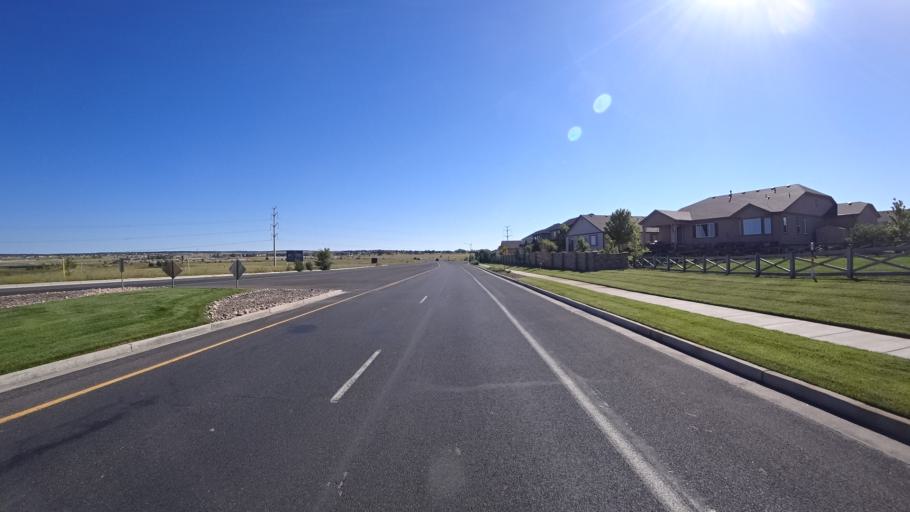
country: US
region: Colorado
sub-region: El Paso County
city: Cimarron Hills
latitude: 38.9358
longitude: -104.6814
